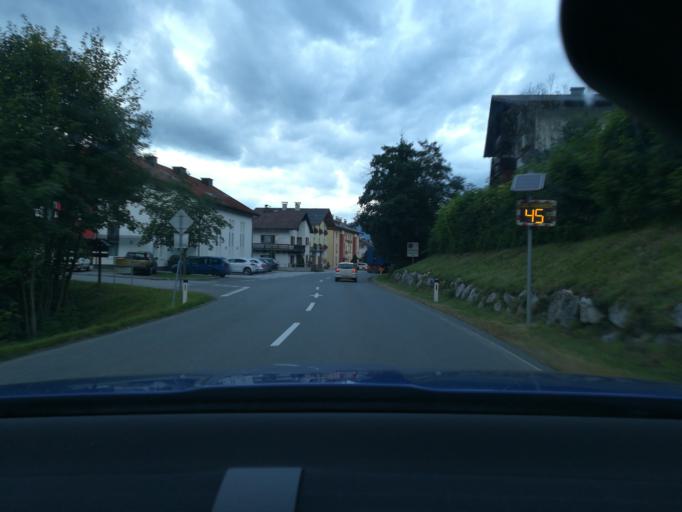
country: AT
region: Salzburg
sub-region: Politischer Bezirk Hallein
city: Abtenau
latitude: 47.5603
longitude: 13.3513
